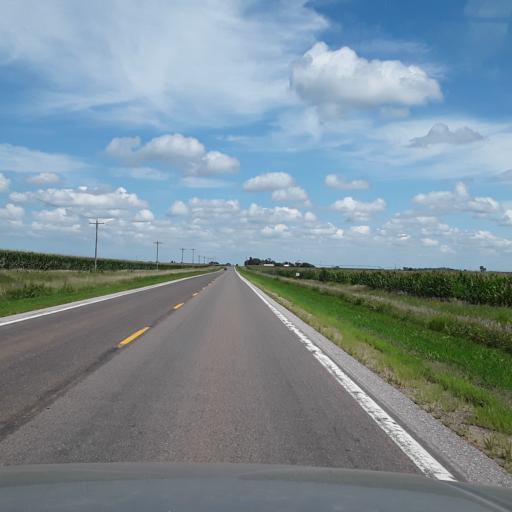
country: US
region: Nebraska
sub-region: Polk County
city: Osceola
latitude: 41.0543
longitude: -97.4063
